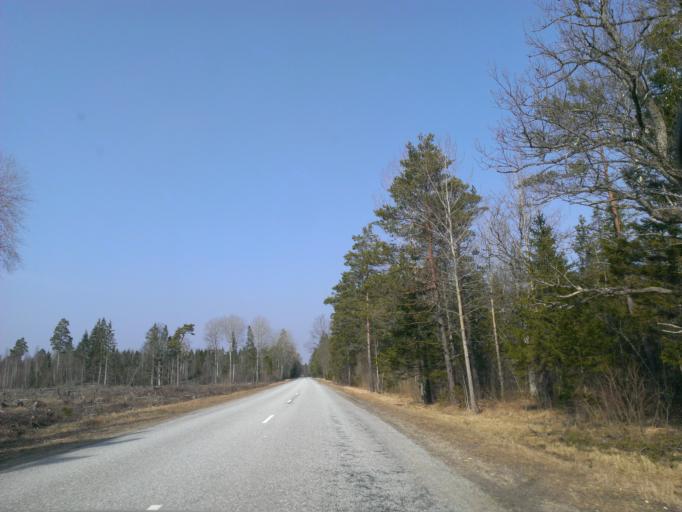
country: EE
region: Saare
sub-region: Kuressaare linn
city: Kuressaare
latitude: 58.3602
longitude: 22.6715
